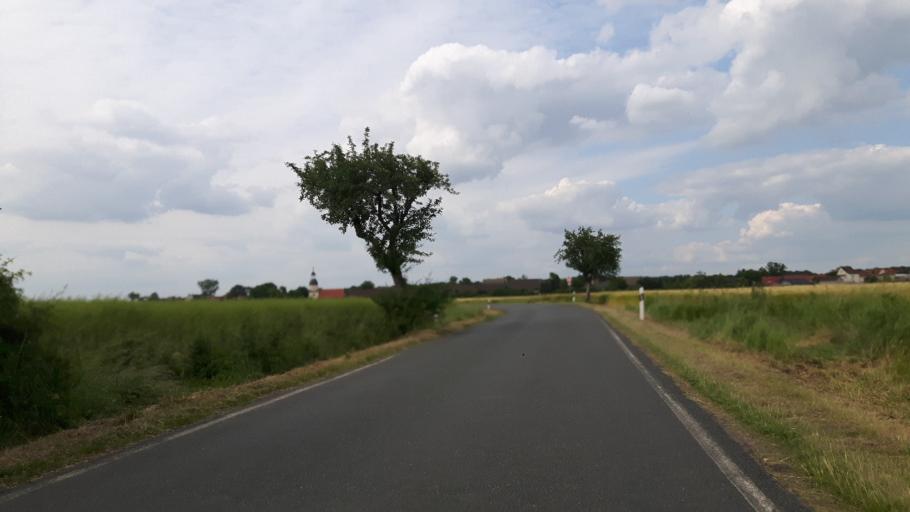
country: DE
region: Saxony-Anhalt
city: Bergwitz
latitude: 51.8124
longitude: 12.5733
